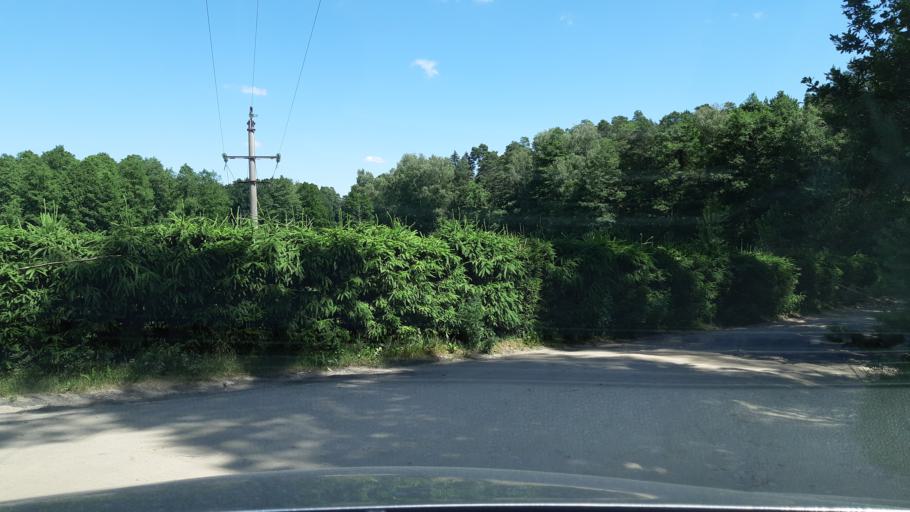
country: PL
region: Warmian-Masurian Voivodeship
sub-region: Powiat piski
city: Ruciane-Nida
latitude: 53.7125
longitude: 21.4893
